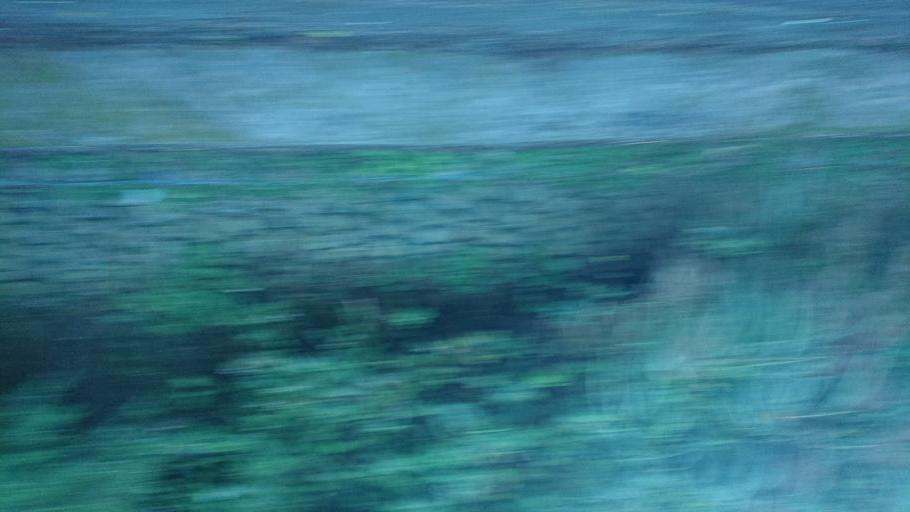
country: TW
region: Taiwan
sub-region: Chiayi
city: Jiayi Shi
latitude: 23.5179
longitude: 120.6243
